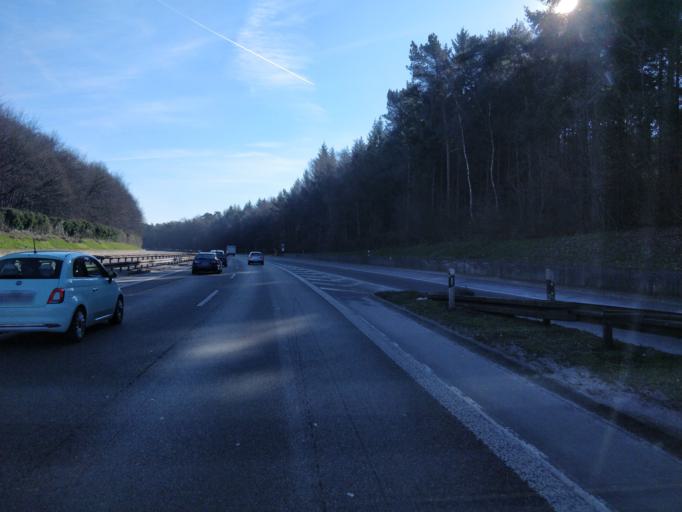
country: DE
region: North Rhine-Westphalia
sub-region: Regierungsbezirk Koln
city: Rath
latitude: 50.9471
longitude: 7.1003
